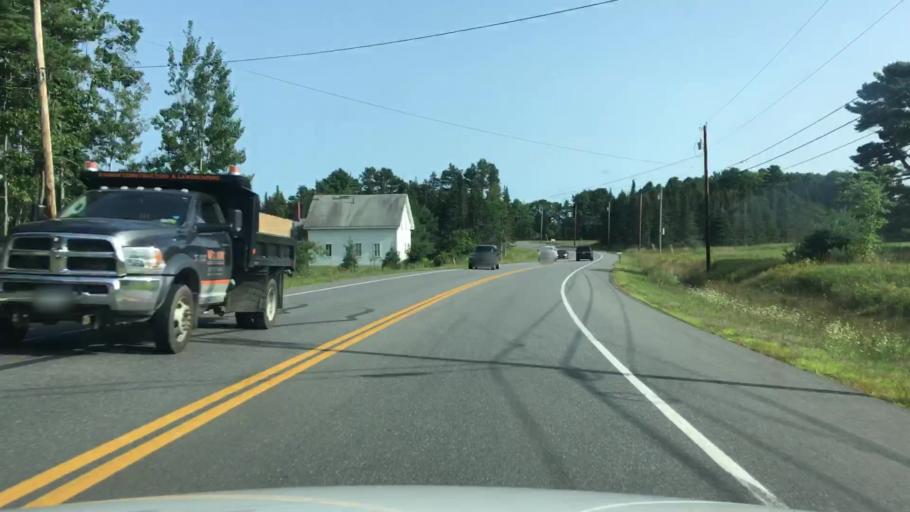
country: US
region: Maine
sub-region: Knox County
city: Warren
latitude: 44.0890
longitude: -69.2335
